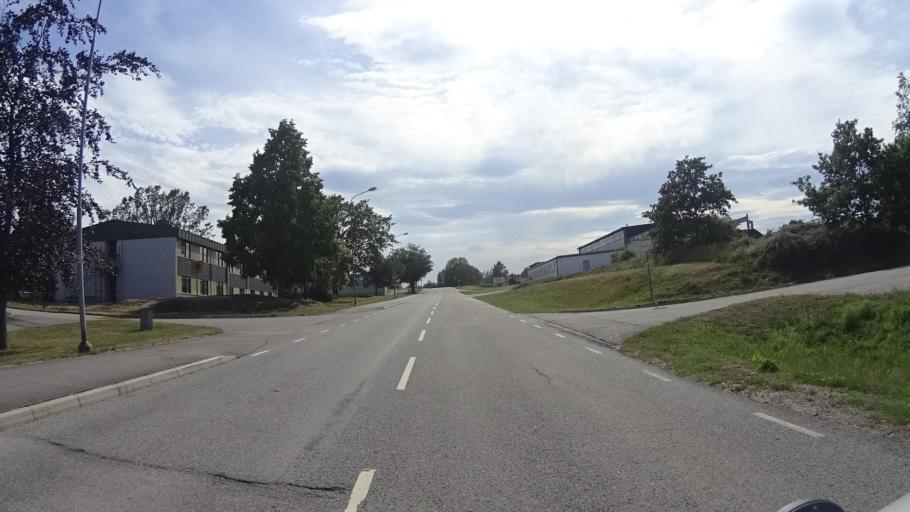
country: SE
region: Kalmar
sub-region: Vasterviks Kommun
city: Gamleby
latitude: 57.8904
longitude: 16.4147
